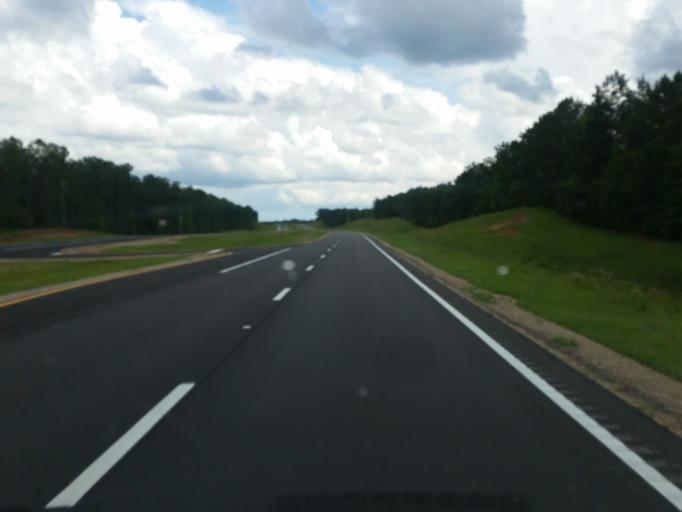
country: US
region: Mississippi
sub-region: Greene County
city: Leakesville
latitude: 31.0646
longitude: -88.7372
